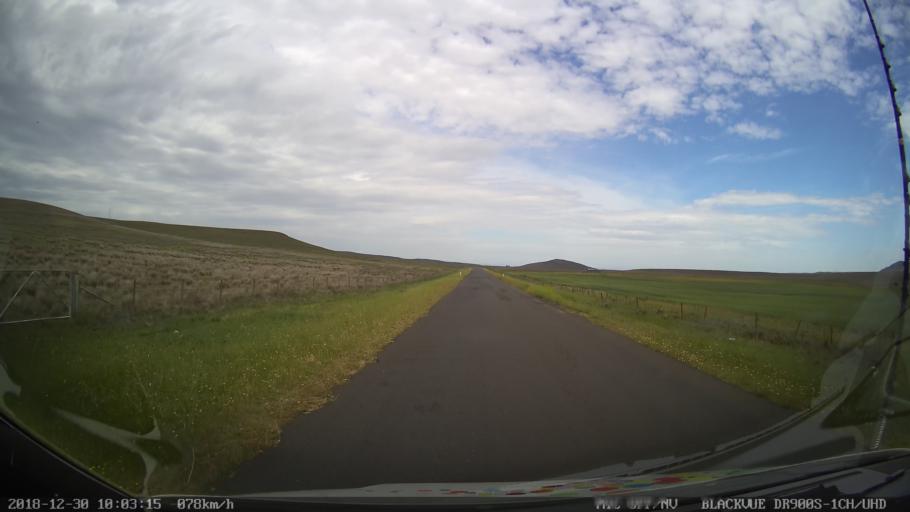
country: AU
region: New South Wales
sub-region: Cooma-Monaro
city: Cooma
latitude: -36.5153
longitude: 149.1601
